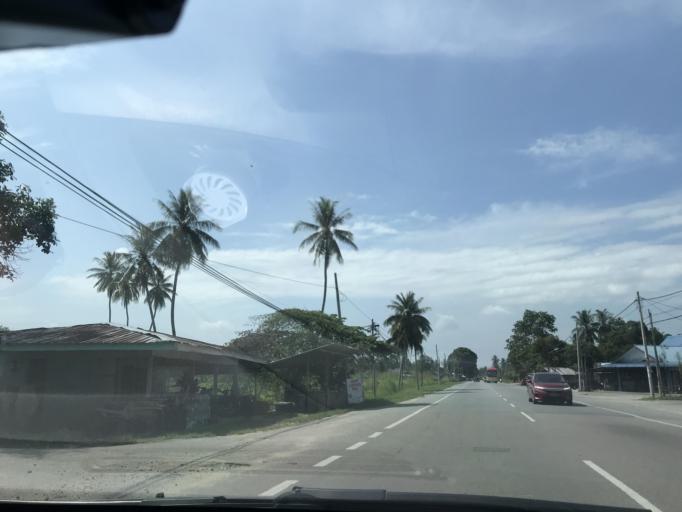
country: MY
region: Kelantan
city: Tumpat
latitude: 6.1457
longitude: 102.1643
